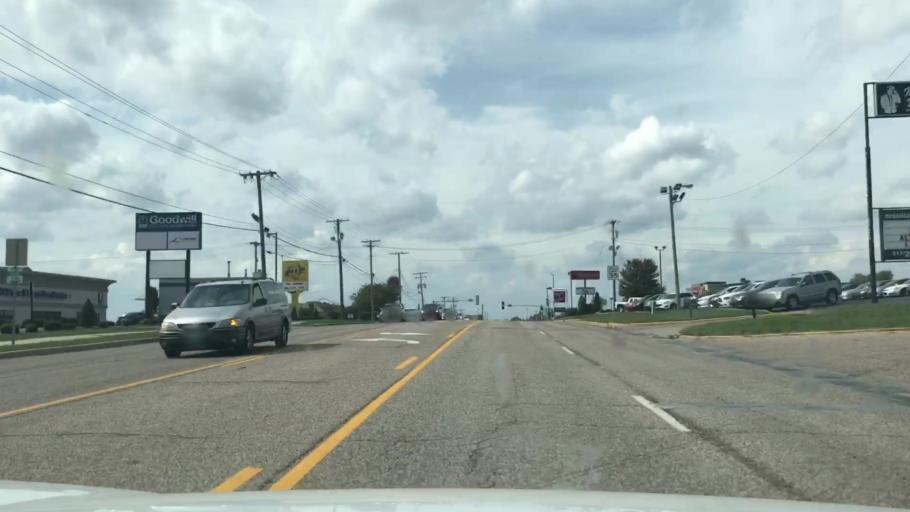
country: US
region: Illinois
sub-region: Adams County
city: Quincy
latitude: 39.9352
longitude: -91.3524
